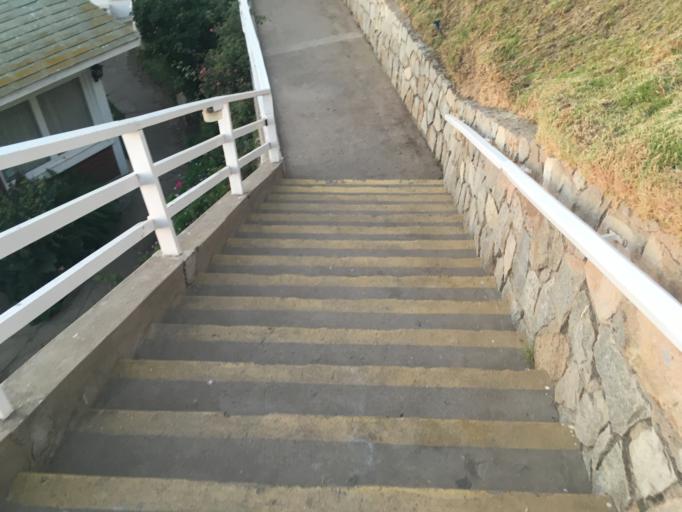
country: CL
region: Valparaiso
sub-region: Provincia de Valparaiso
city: Vina del Mar
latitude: -32.9186
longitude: -71.5195
